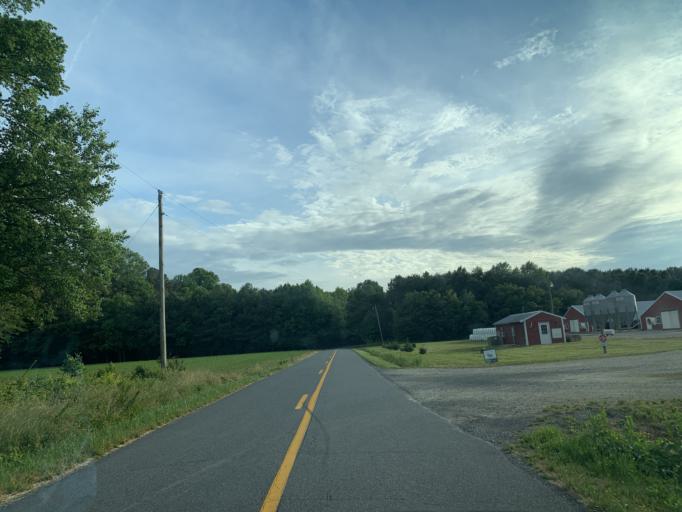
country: US
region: Maryland
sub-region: Worcester County
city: Snow Hill
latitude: 38.0952
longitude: -75.4585
